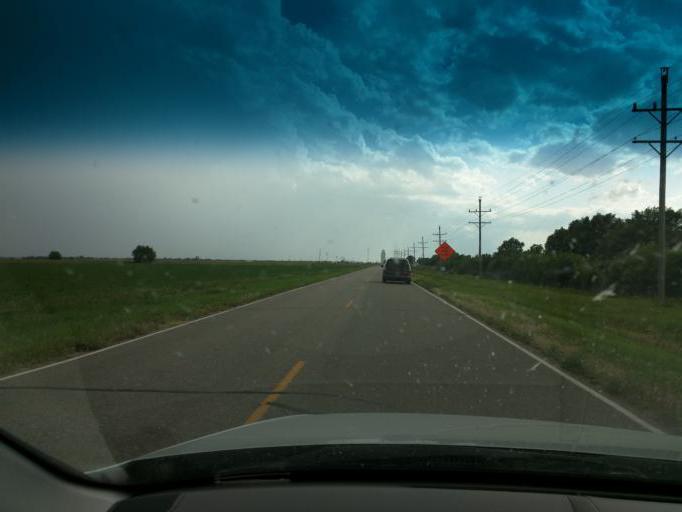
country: US
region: Kansas
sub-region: Reno County
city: South Hutchinson
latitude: 38.0165
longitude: -97.9977
